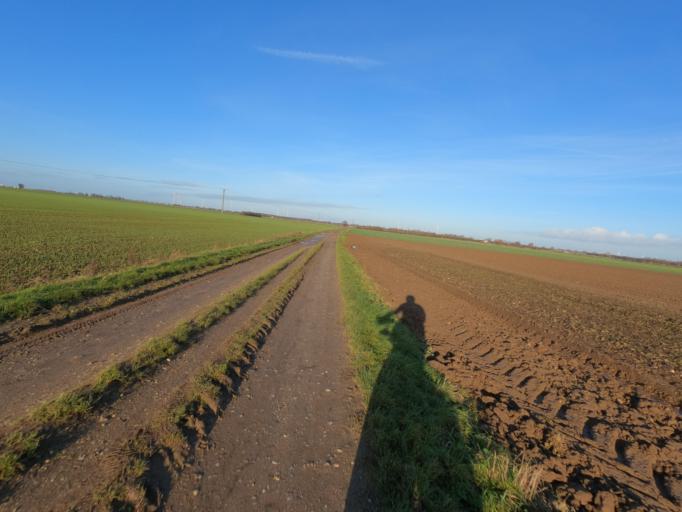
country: DE
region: North Rhine-Westphalia
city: Julich
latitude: 50.9394
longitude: 6.3968
